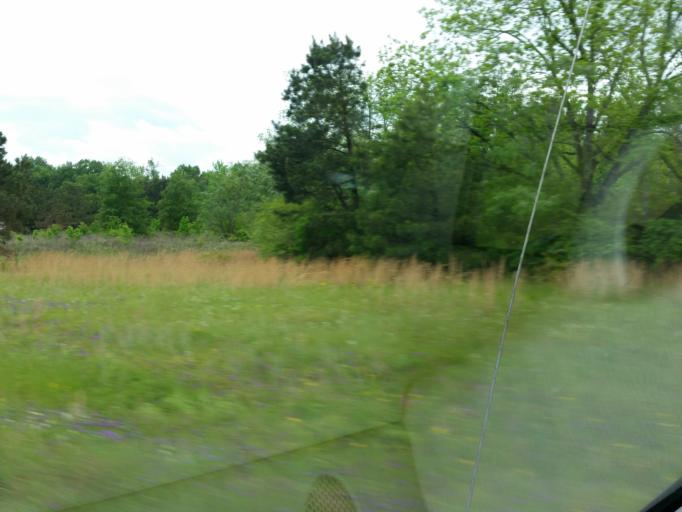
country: US
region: Georgia
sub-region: Peach County
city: Byron
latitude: 32.6805
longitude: -83.8420
